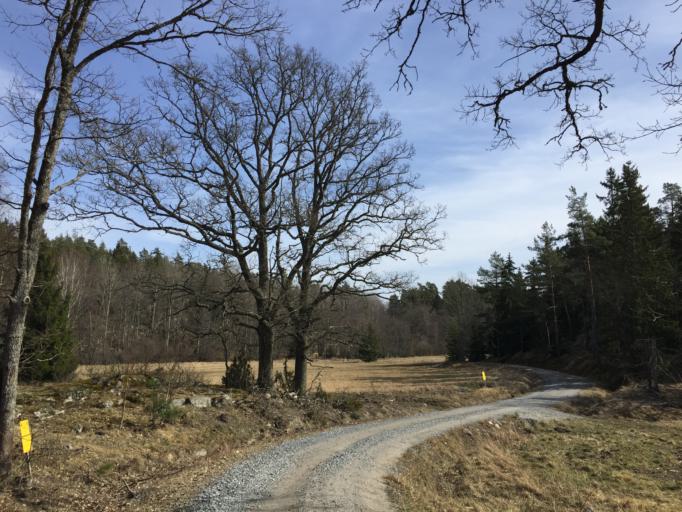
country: SE
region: Stockholm
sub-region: Salems Kommun
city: Ronninge
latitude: 59.2519
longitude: 17.6836
